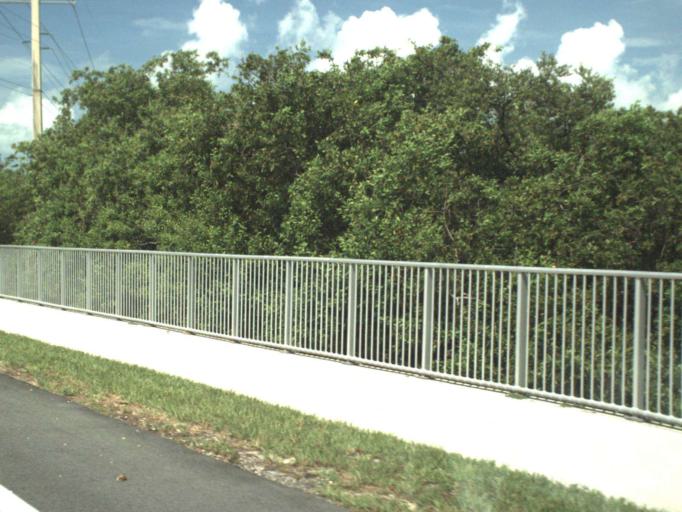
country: US
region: Florida
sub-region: Monroe County
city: Islamorada
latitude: 24.8501
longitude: -80.7393
